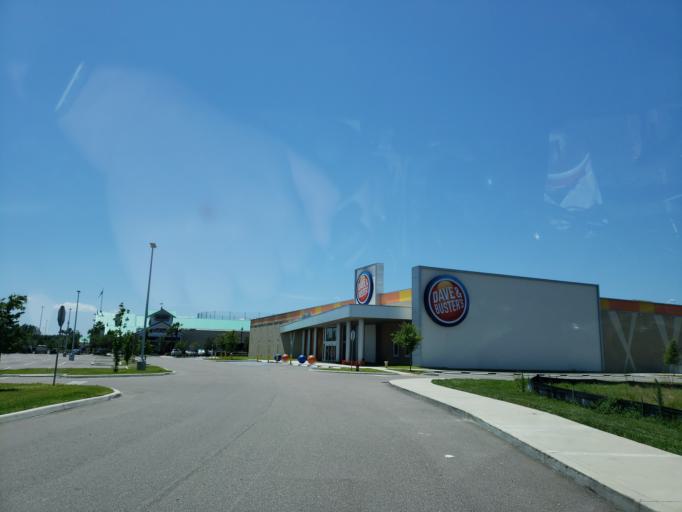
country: US
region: Florida
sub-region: Hillsborough County
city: Palm River-Clair Mel
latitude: 27.9367
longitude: -82.3342
